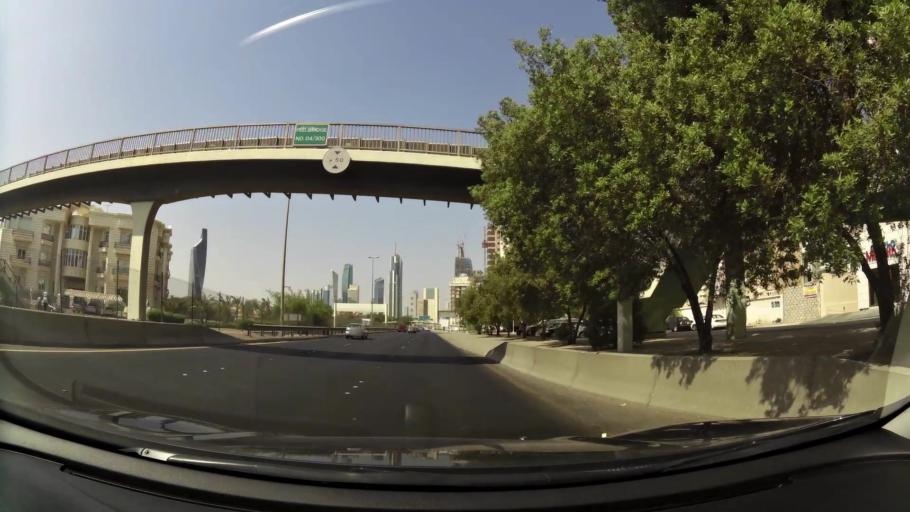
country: KW
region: Al Asimah
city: Ad Dasmah
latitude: 29.3697
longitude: 48.0042
